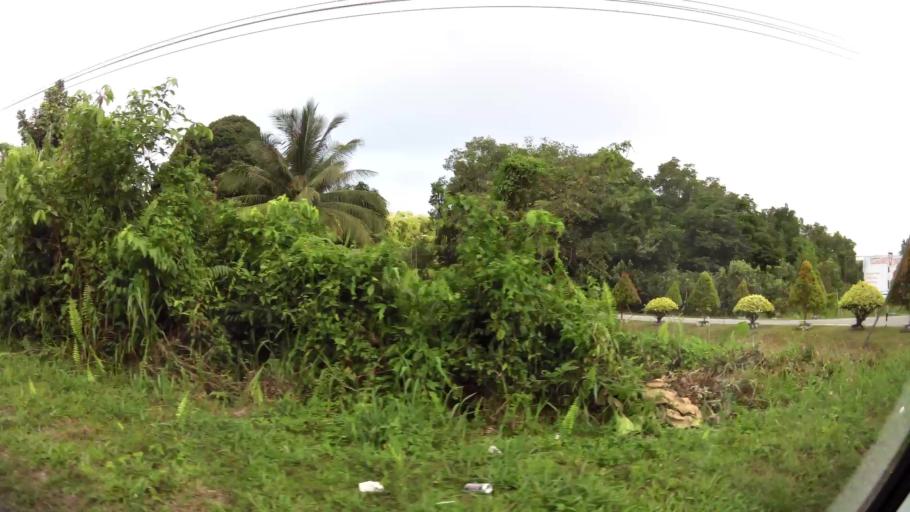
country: BN
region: Brunei and Muara
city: Bandar Seri Begawan
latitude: 4.9131
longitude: 115.0023
